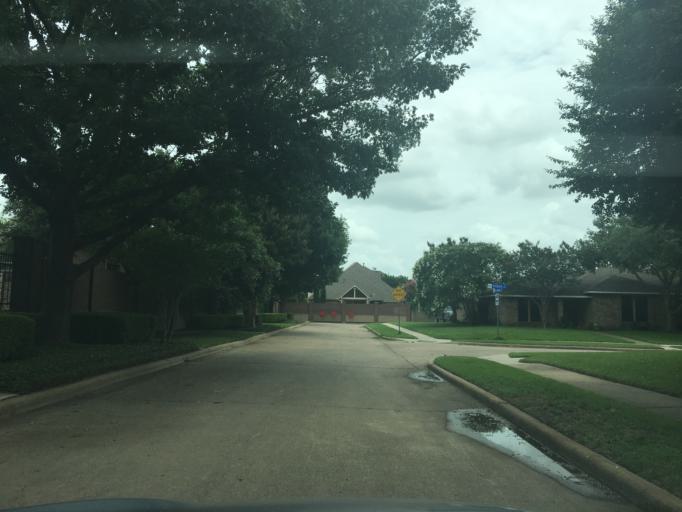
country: US
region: Texas
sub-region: Dallas County
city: Richardson
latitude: 32.9319
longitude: -96.7207
